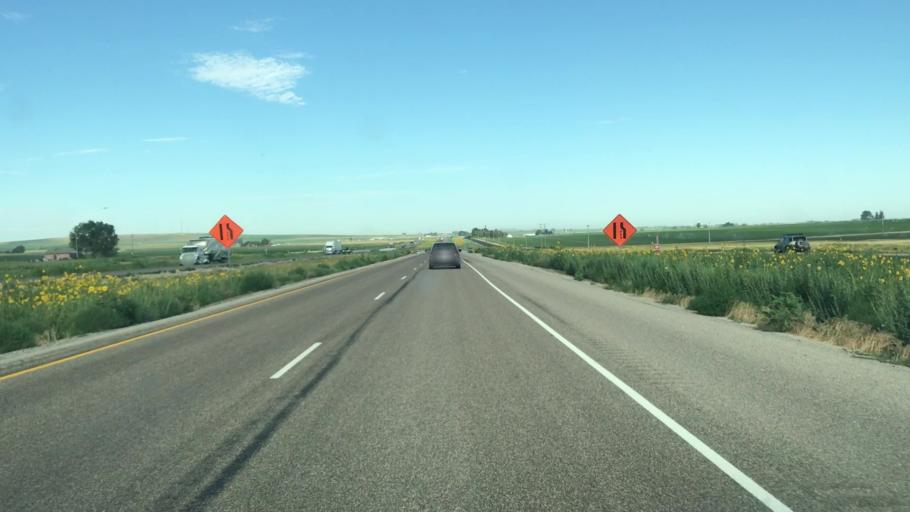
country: US
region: Idaho
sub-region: Cassia County
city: Burley
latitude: 42.5764
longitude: -114.0254
